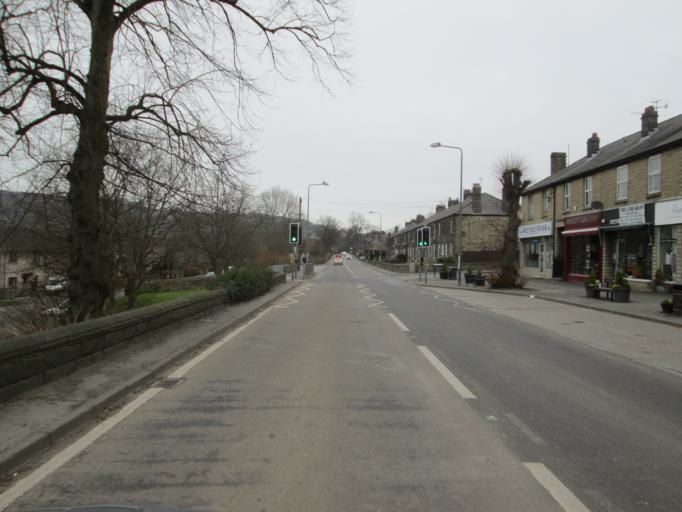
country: GB
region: England
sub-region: Derbyshire
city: Matlock
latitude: 53.1650
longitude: -1.5952
